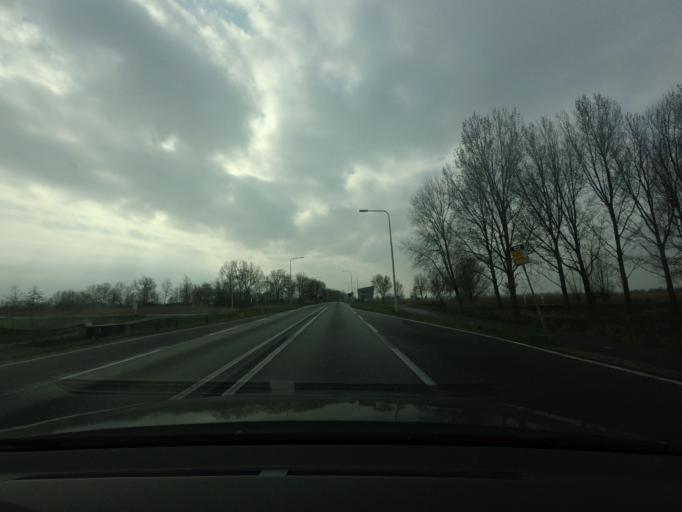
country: NL
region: Utrecht
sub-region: Gemeente De Ronde Venen
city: Mijdrecht
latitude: 52.1624
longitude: 4.9086
